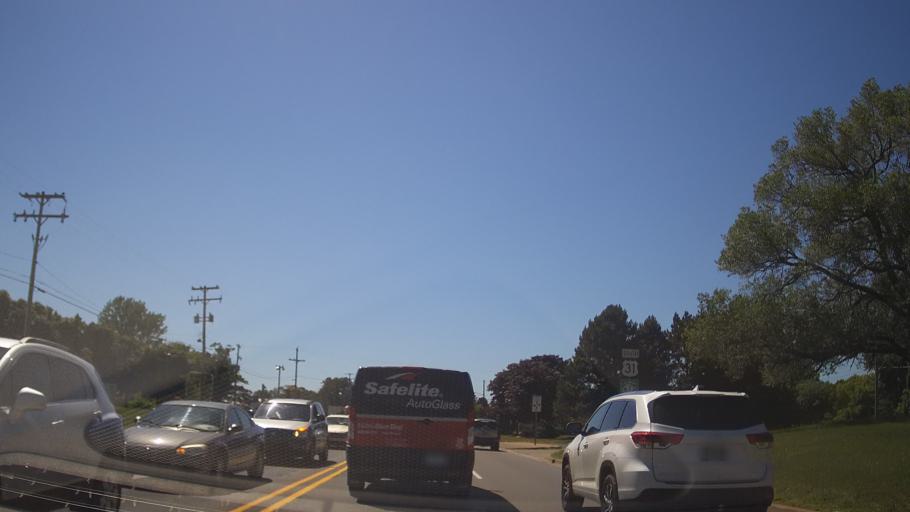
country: US
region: Michigan
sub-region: Emmet County
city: Petoskey
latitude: 45.3893
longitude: -84.9129
